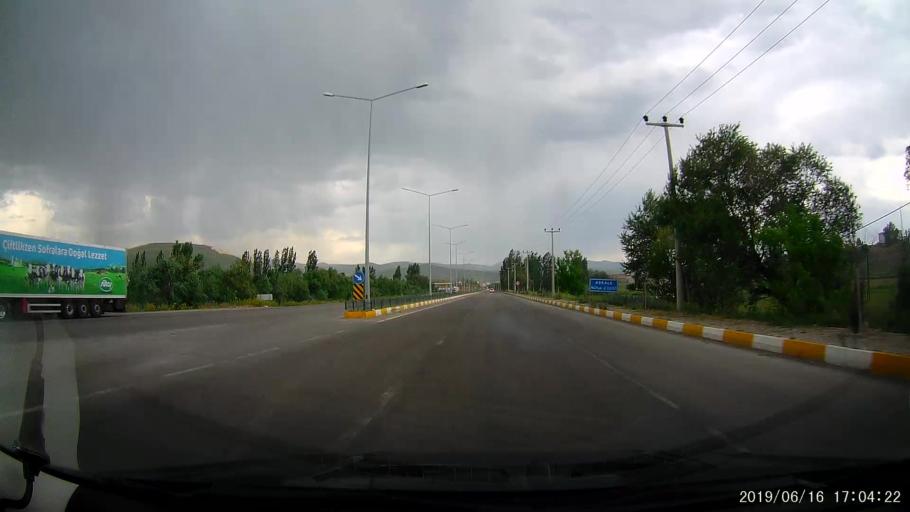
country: TR
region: Erzurum
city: Askale
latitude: 39.9265
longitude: 40.7104
